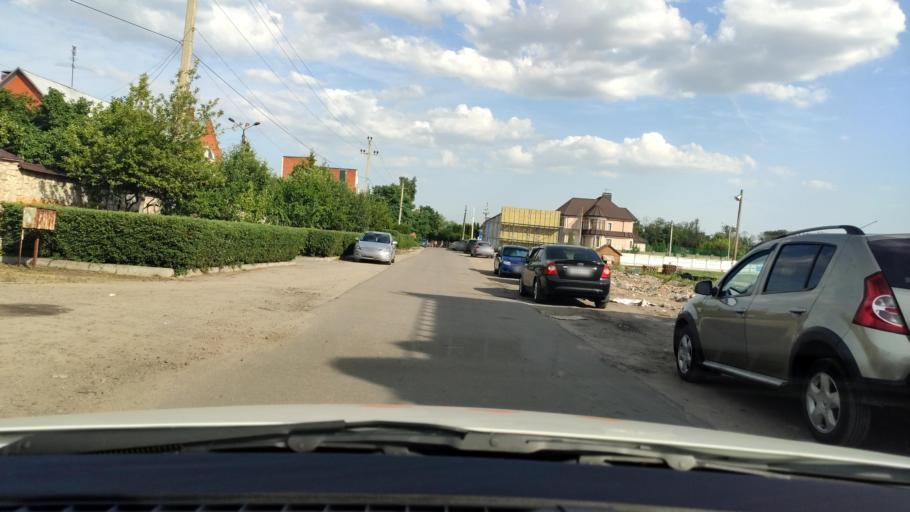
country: RU
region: Voronezj
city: Novaya Usman'
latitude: 51.6306
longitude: 39.4160
